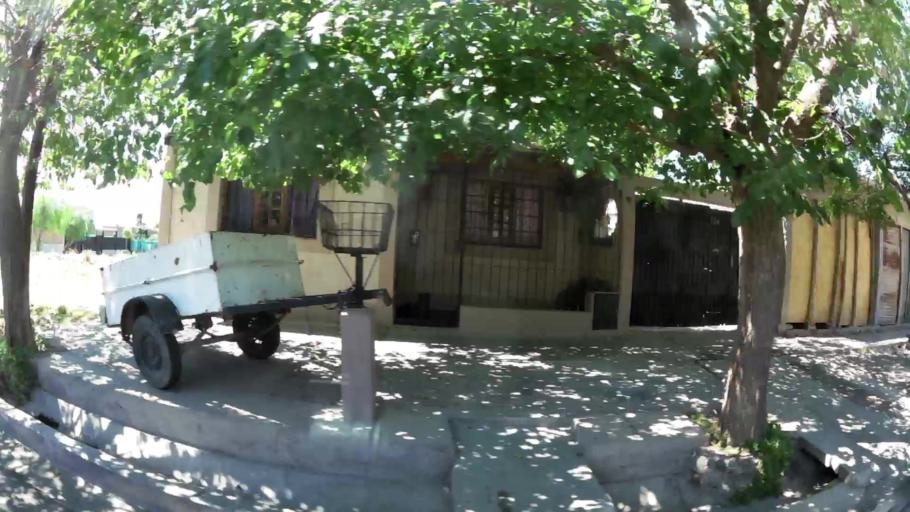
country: AR
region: Mendoza
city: Las Heras
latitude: -32.8488
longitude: -68.8713
